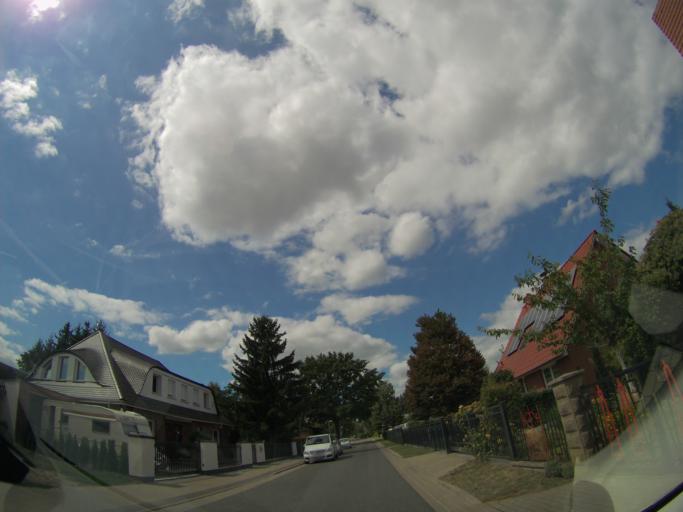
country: DE
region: Brandenburg
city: Stahnsdorf
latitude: 52.3778
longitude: 13.2030
